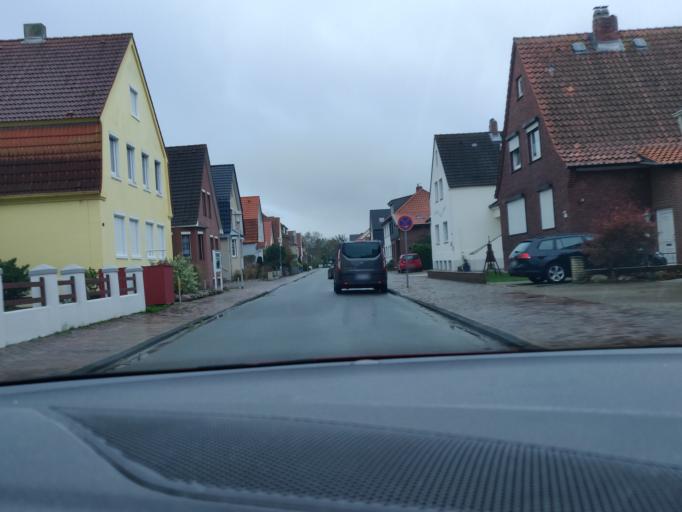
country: DE
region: Lower Saxony
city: Cuxhaven
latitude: 53.8866
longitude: 8.6763
